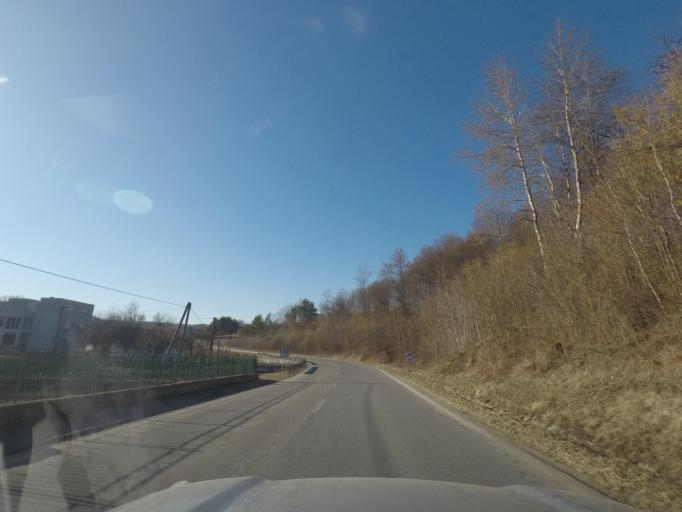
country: SK
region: Presovsky
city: Medzilaborce
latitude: 49.2486
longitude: 21.9276
